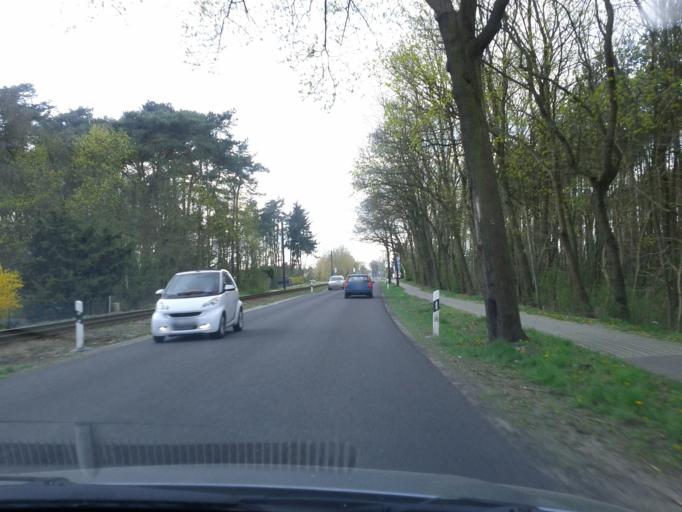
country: DE
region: Brandenburg
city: Woltersdorf
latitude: 52.4721
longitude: 13.7406
